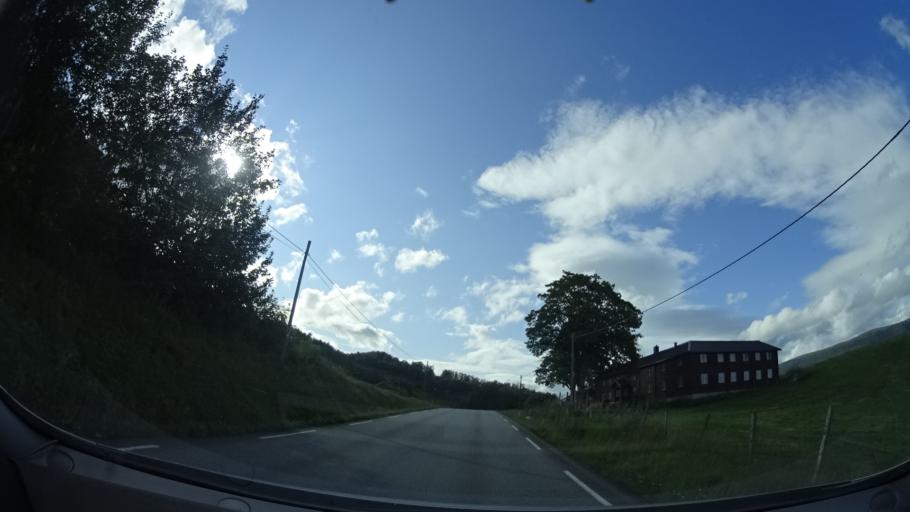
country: NO
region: More og Romsdal
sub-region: Aure
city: Aure
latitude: 63.1340
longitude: 8.4991
